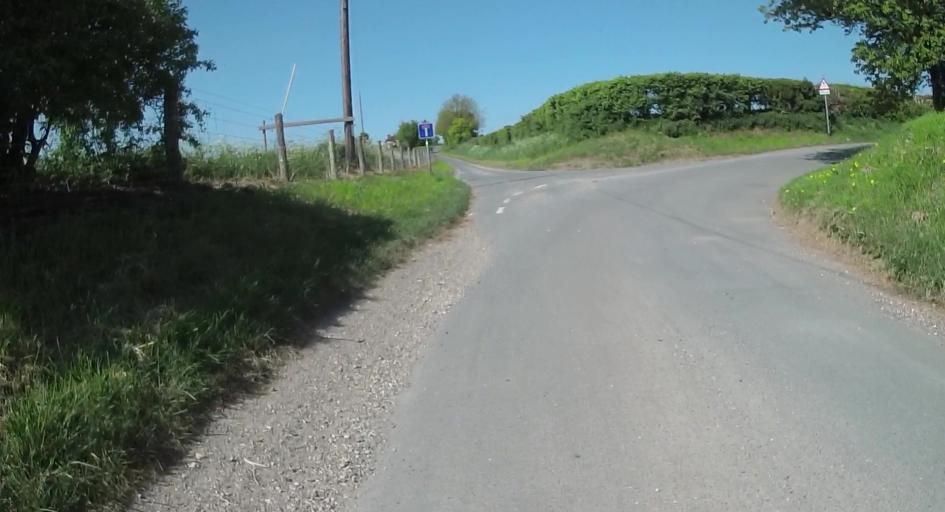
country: GB
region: England
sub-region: Hampshire
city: Kings Worthy
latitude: 51.1514
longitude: -1.2854
